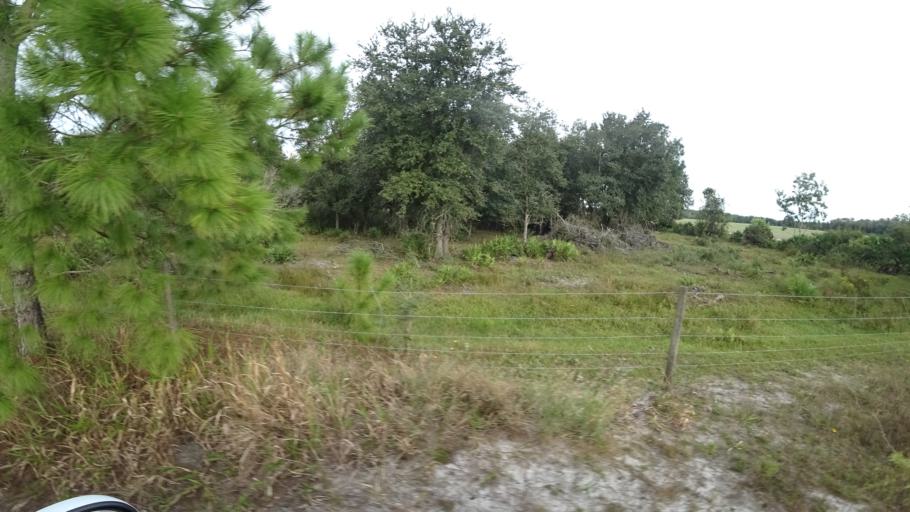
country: US
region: Florida
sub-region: Hillsborough County
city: Wimauma
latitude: 27.5669
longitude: -82.0819
